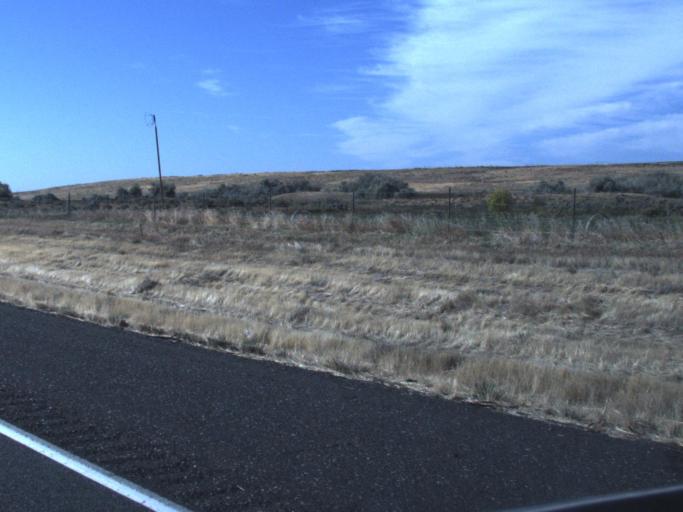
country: US
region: Washington
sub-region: Franklin County
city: Basin City
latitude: 46.4426
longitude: -119.0204
